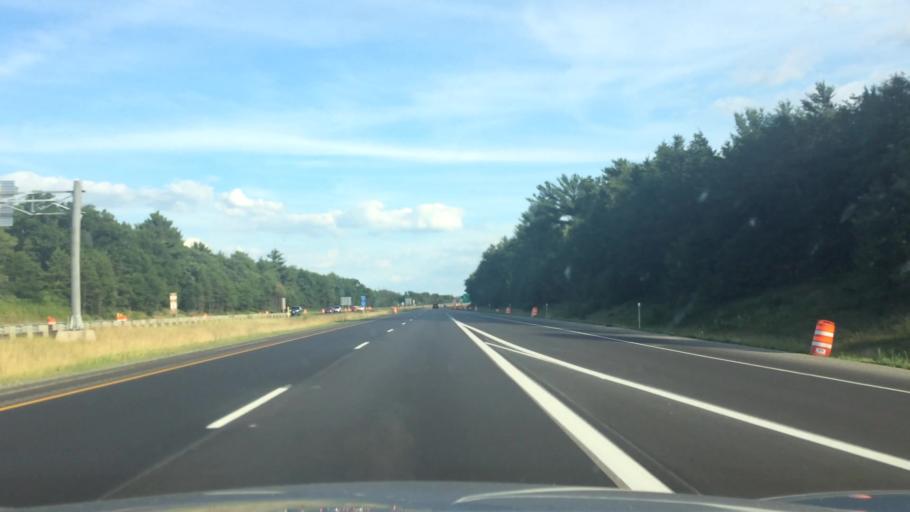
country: US
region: Wisconsin
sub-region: Portage County
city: Whiting
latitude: 44.5208
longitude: -89.5251
